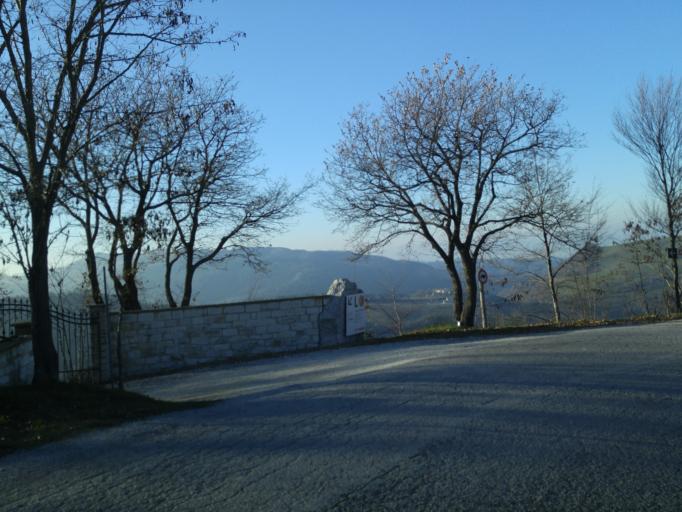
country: IT
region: The Marches
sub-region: Provincia di Pesaro e Urbino
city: Isola del Piano
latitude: 43.7214
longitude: 12.7478
